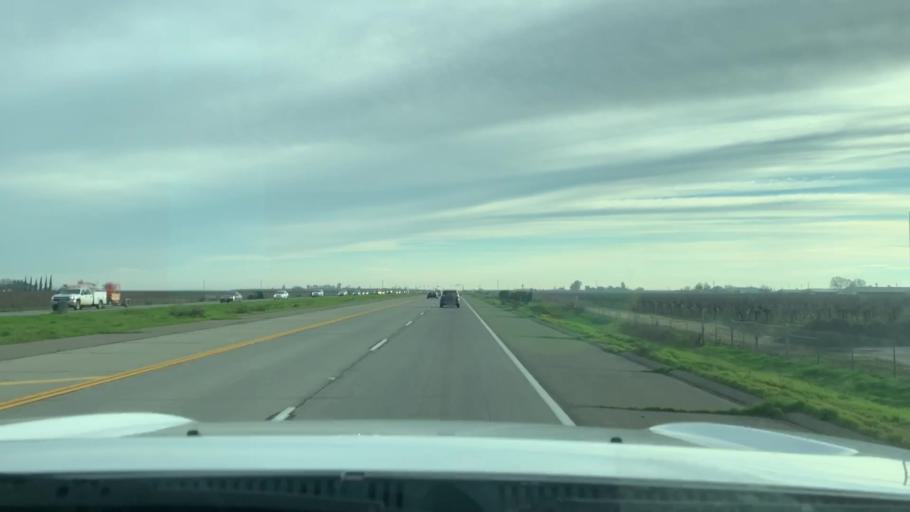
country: US
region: California
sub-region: Fresno County
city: Caruthers
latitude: 36.5549
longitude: -119.7863
